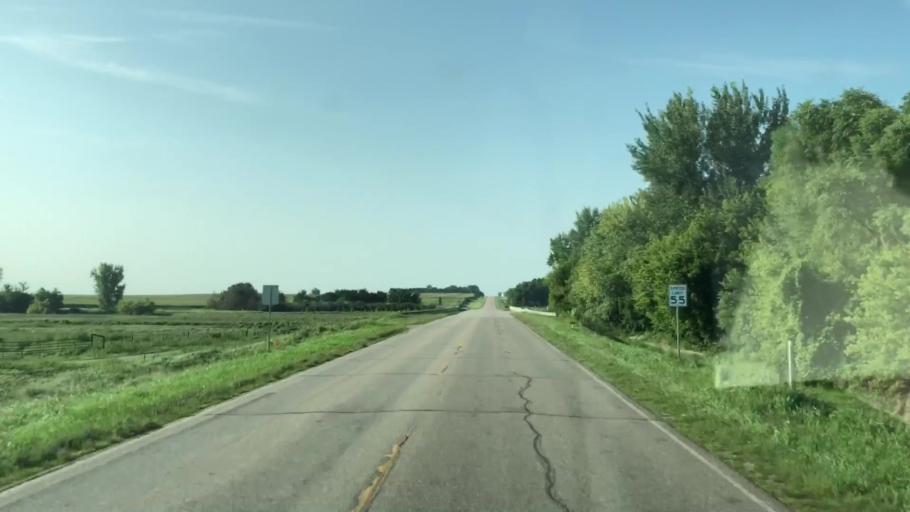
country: US
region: Iowa
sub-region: Lyon County
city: George
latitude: 43.3344
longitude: -95.9987
